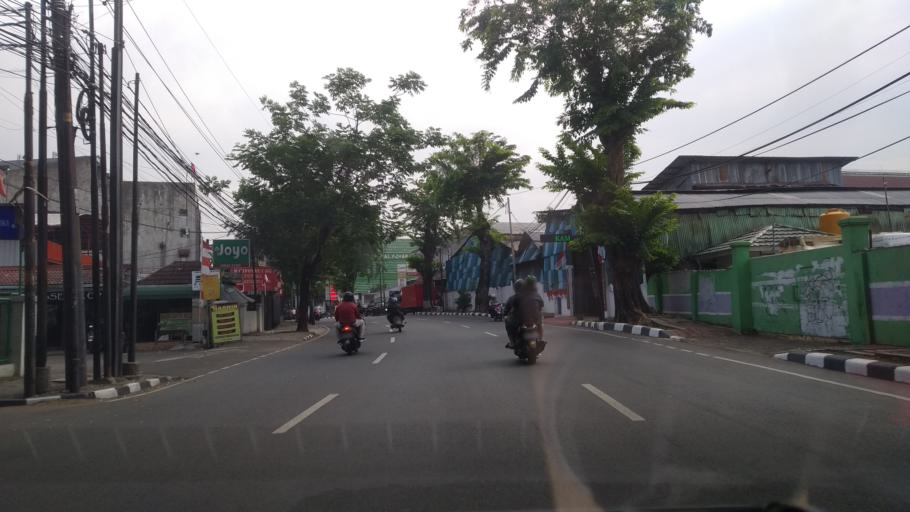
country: ID
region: Banten
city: South Tangerang
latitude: -6.2529
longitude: 106.7789
